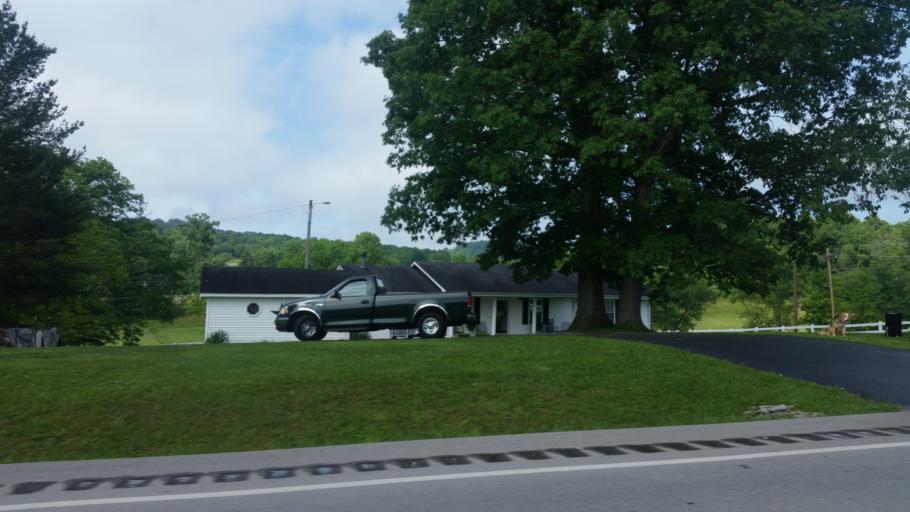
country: US
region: Kentucky
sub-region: Rowan County
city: Morehead
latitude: 38.2399
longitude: -83.5094
